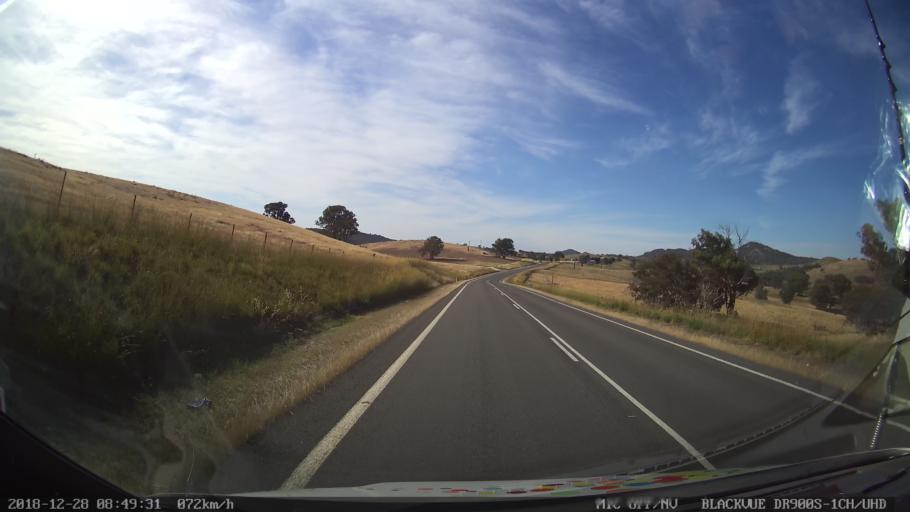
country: AU
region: New South Wales
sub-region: Upper Lachlan Shire
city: Crookwell
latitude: -34.0464
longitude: 149.3372
